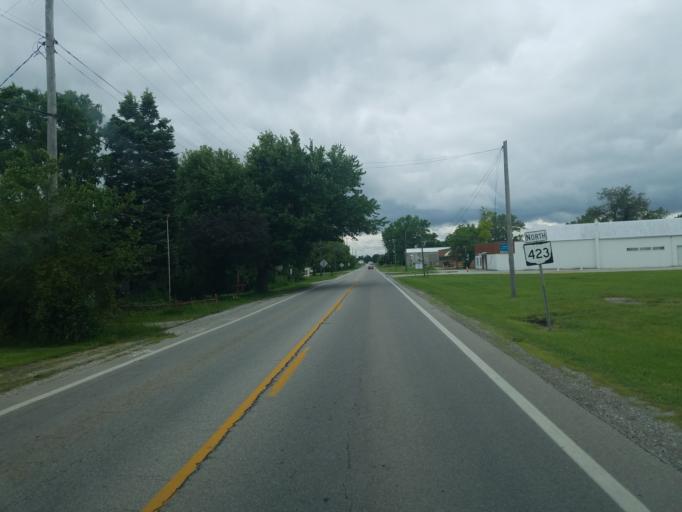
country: US
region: Ohio
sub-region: Marion County
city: Marion
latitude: 40.6199
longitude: -83.1321
